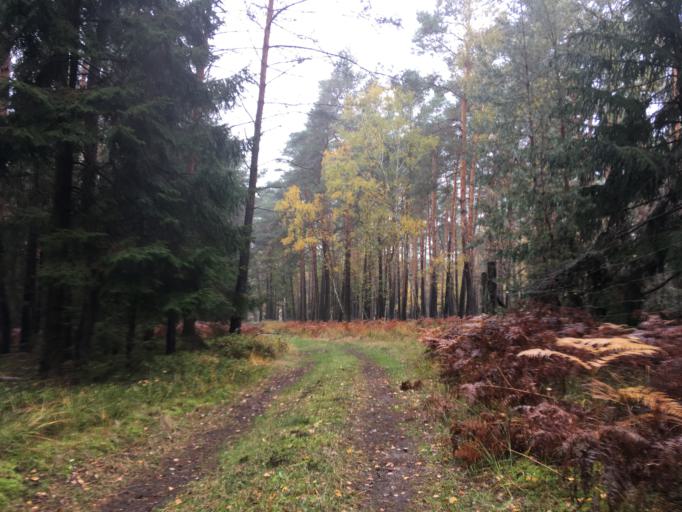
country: DE
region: Brandenburg
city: Beeskow
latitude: 52.2270
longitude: 14.2931
